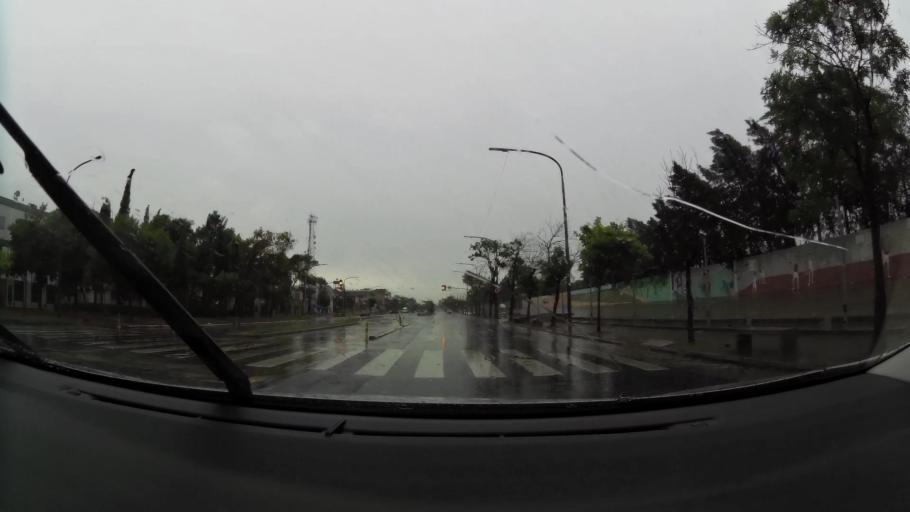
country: AR
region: Buenos Aires F.D.
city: Villa Lugano
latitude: -34.6519
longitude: -58.4332
